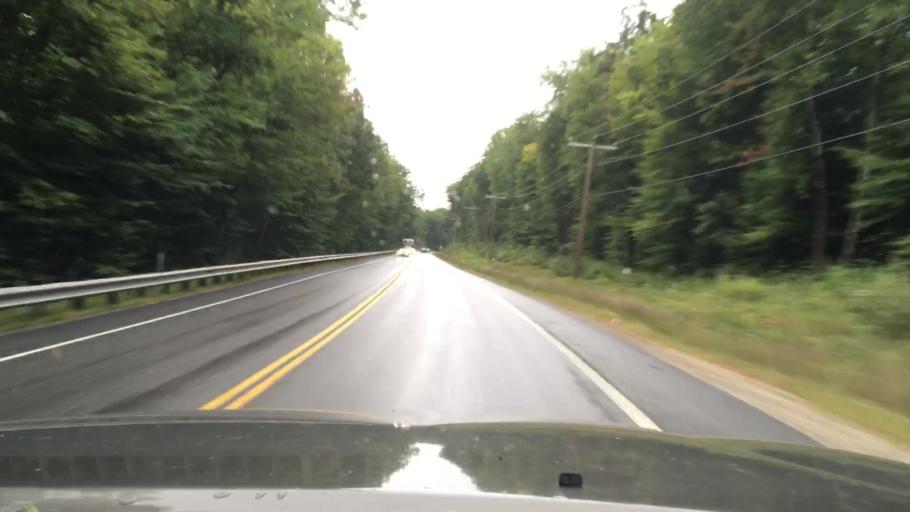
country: US
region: New Hampshire
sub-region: Hillsborough County
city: Antrim
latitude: 43.0886
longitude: -71.9672
